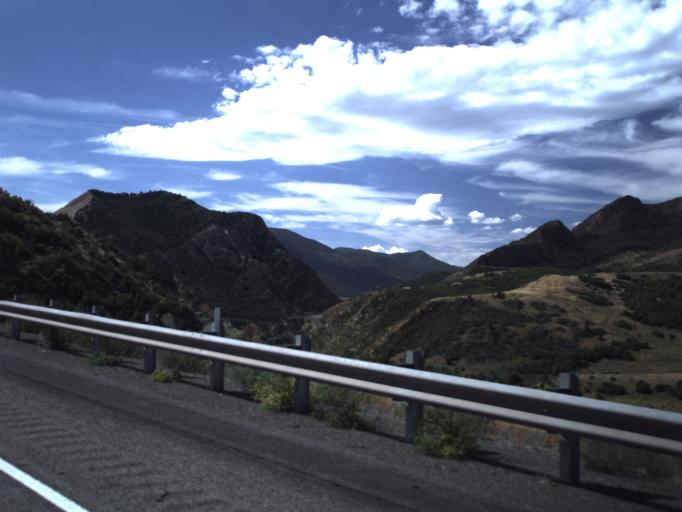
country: US
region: Utah
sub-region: Utah County
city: Mapleton
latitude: 40.0177
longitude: -111.4957
